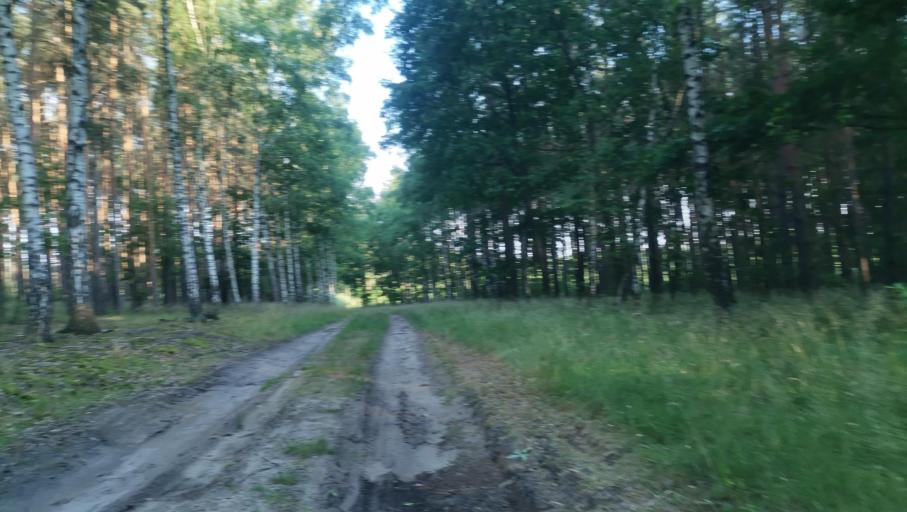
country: PL
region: Greater Poland Voivodeship
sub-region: Powiat jarocinski
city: Witaszyce
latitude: 51.9800
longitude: 17.5456
